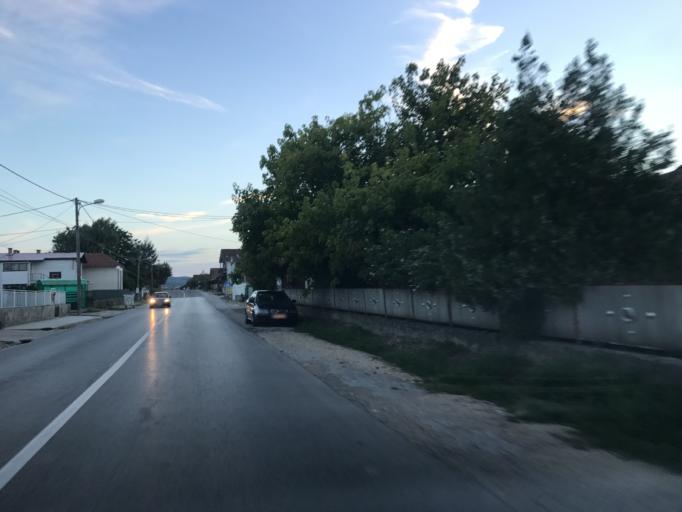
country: RS
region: Central Serbia
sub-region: Branicevski Okrug
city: Veliko Gradiste
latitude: 44.7314
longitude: 21.4682
